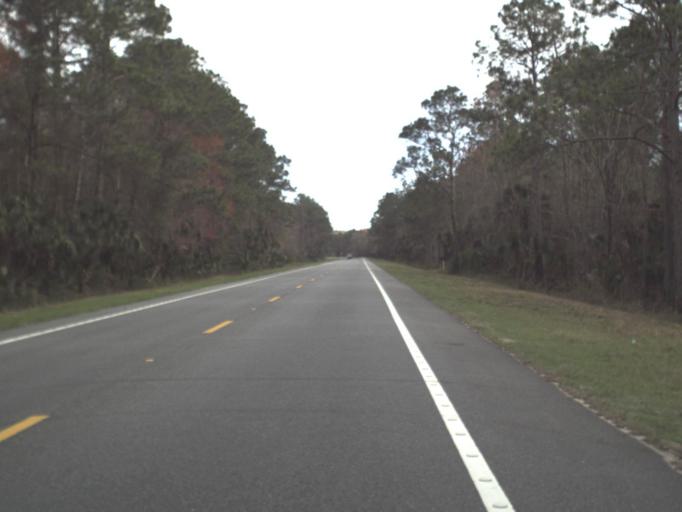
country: US
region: Florida
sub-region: Leon County
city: Woodville
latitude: 30.1689
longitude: -84.0066
